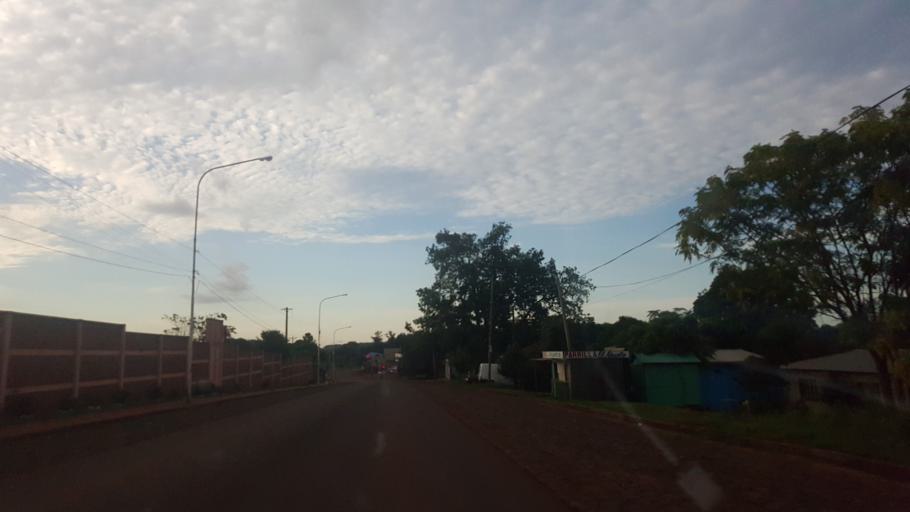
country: AR
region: Misiones
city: Dos de Mayo
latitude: -27.0344
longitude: -54.6854
